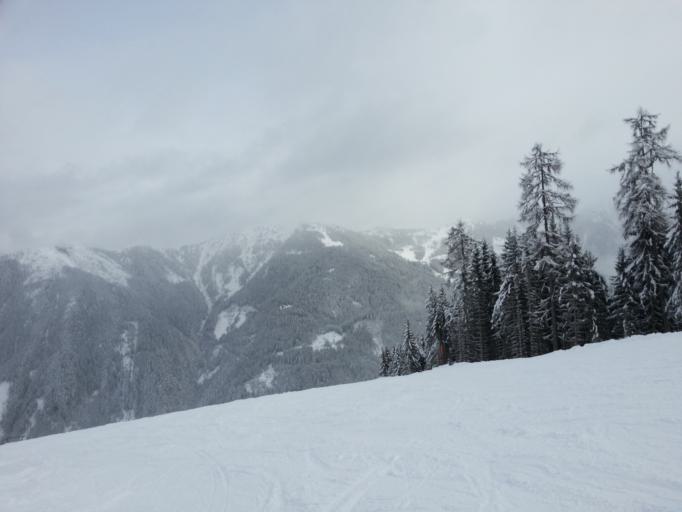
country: AT
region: Salzburg
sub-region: Politischer Bezirk Sankt Johann im Pongau
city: Flachau
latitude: 47.3048
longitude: 13.3714
